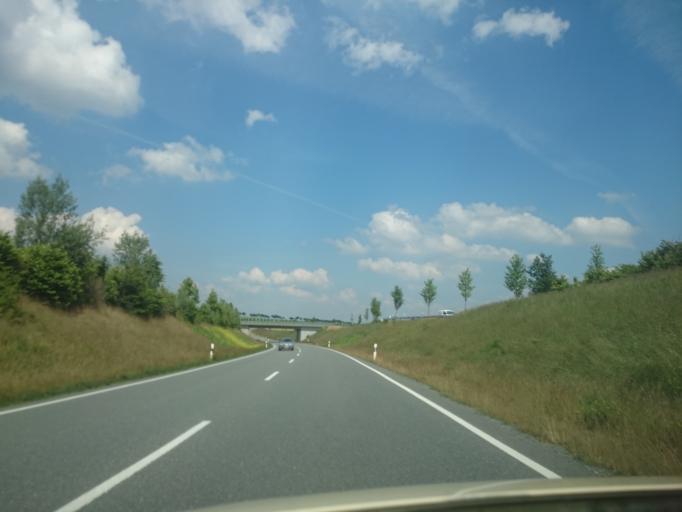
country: DE
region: Saxony
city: Marienberg
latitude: 50.6688
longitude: 13.1433
